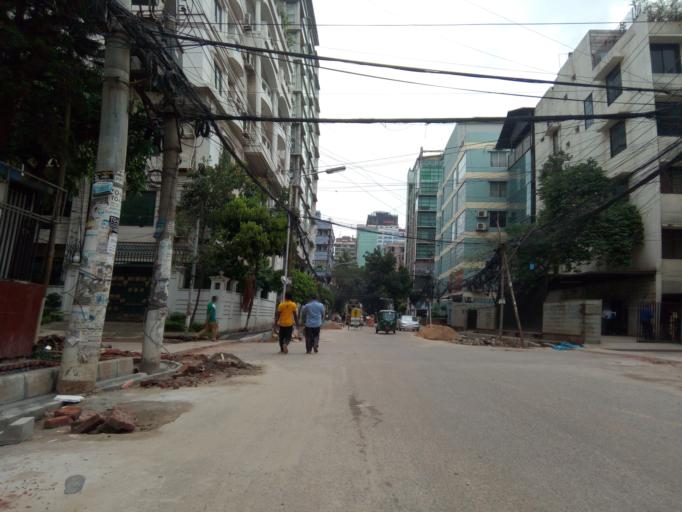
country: BD
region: Dhaka
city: Paltan
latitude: 23.7900
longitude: 90.4039
